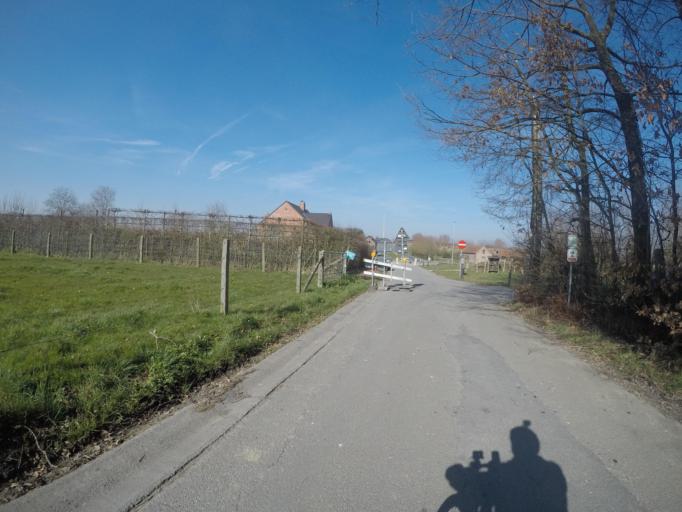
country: BE
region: Flanders
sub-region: Provincie Oost-Vlaanderen
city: Sint-Maria-Lierde
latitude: 50.7886
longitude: 3.8513
